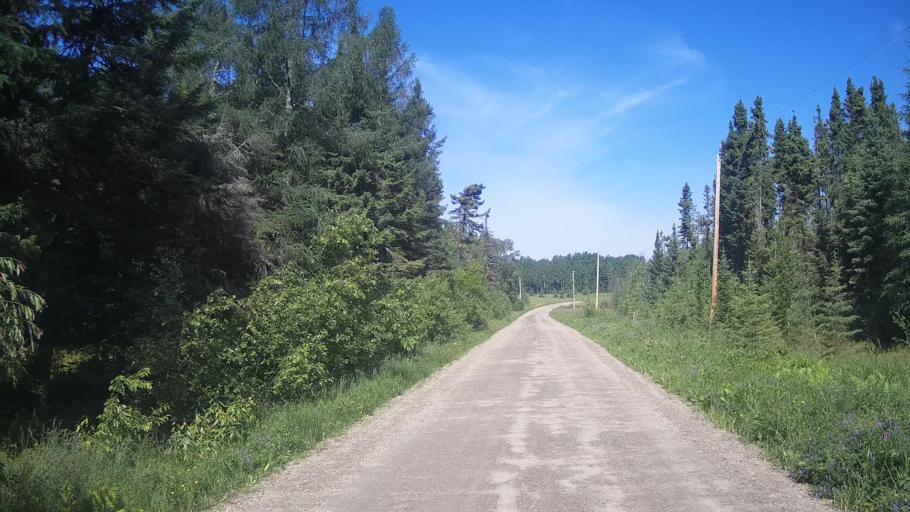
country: CA
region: Ontario
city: Dryden
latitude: 49.8184
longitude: -93.3337
